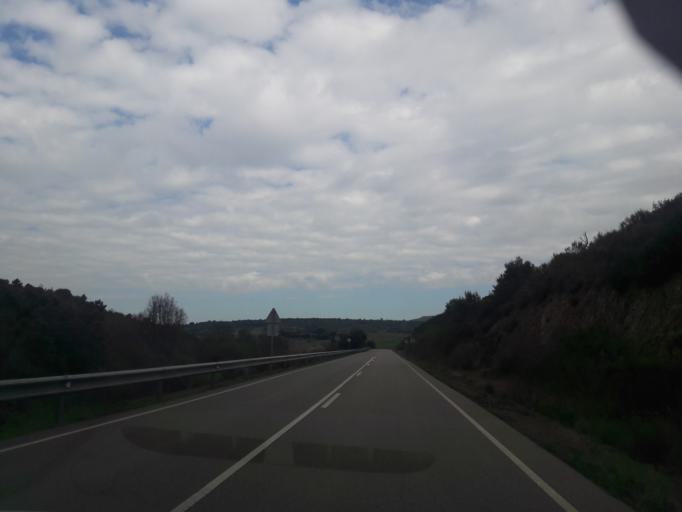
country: ES
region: Castille and Leon
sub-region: Provincia de Salamanca
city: Serradilla del Arroyo
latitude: 40.5164
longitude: -6.3635
